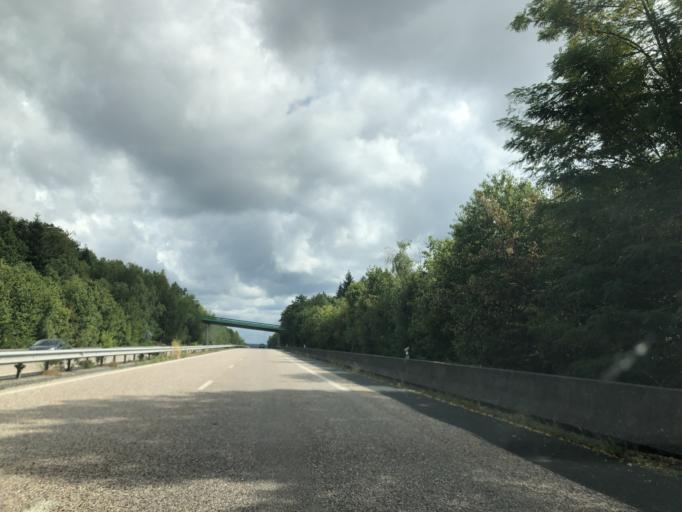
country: FR
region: Lorraine
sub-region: Departement de Meurthe-et-Moselle
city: Baccarat
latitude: 48.4560
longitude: 6.7508
